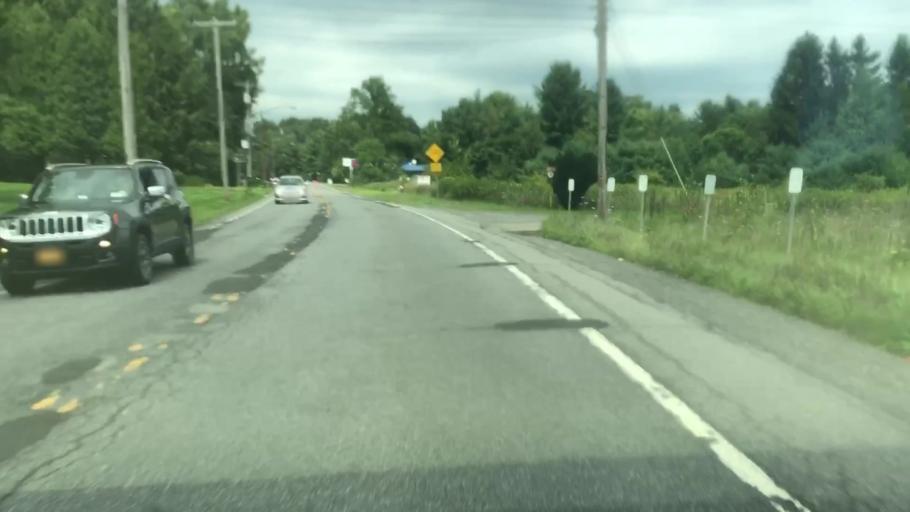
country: US
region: New York
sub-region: Schenectady County
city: Rotterdam
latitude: 42.7339
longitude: -73.9391
